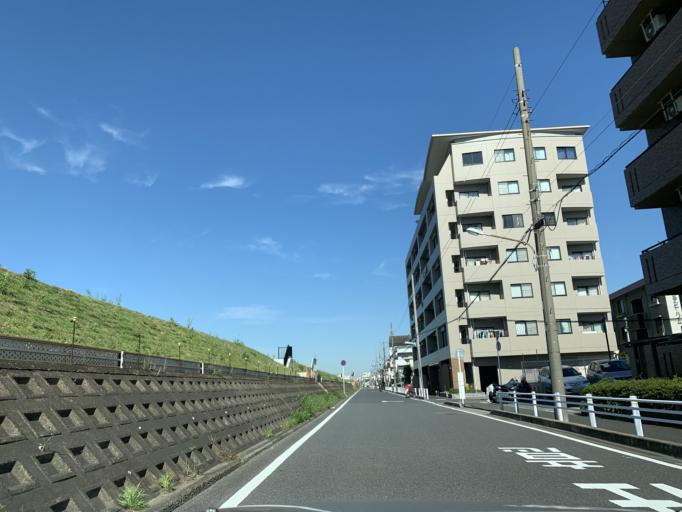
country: JP
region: Tokyo
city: Urayasu
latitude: 35.6494
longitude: 139.8864
